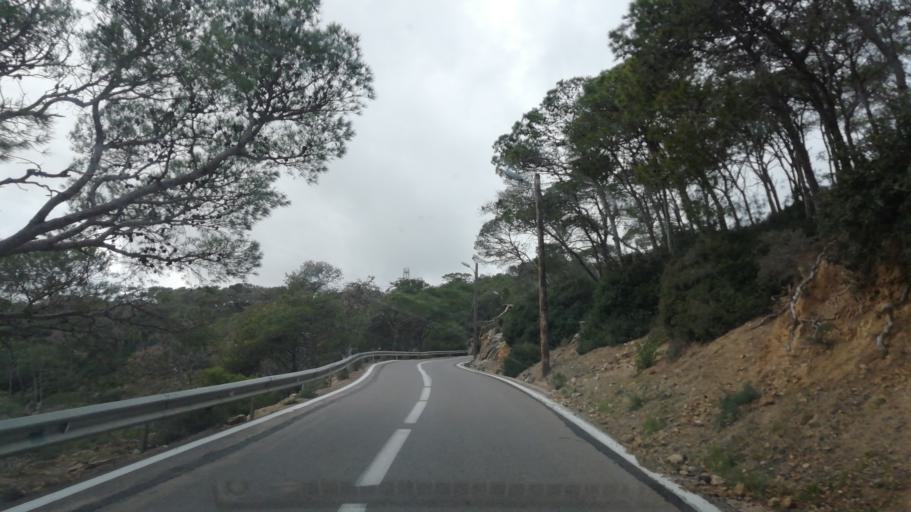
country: DZ
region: Oran
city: Oran
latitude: 35.7032
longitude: -0.6745
